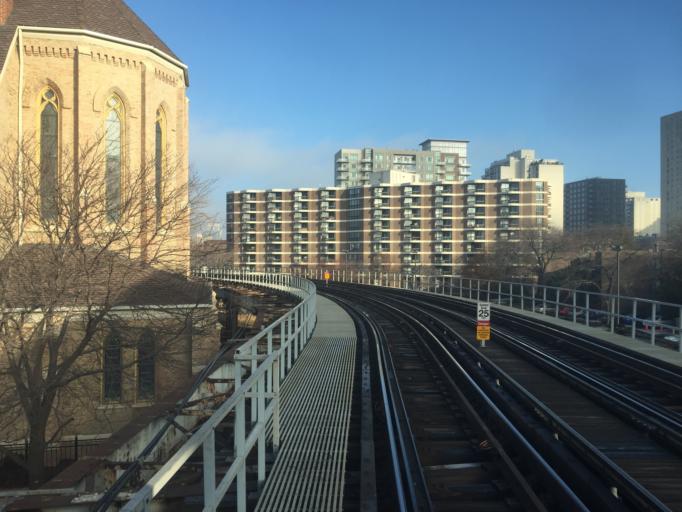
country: US
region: Illinois
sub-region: Cook County
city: Chicago
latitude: 41.9020
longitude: -87.6366
